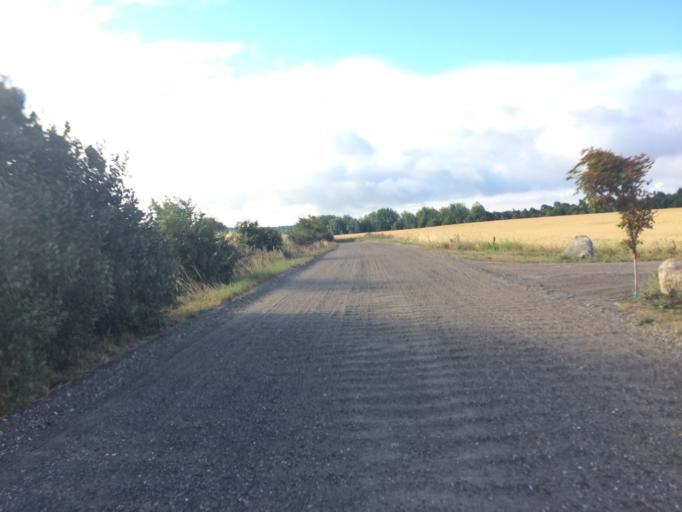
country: DK
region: Central Jutland
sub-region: Skive Kommune
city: Skive
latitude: 56.5889
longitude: 9.0170
